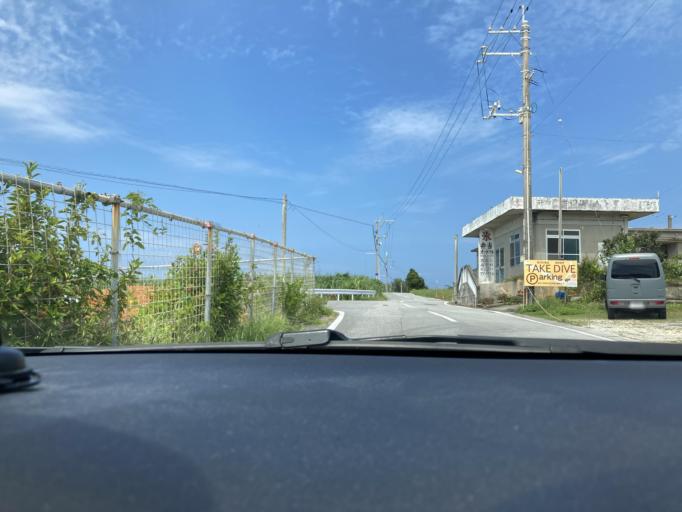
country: JP
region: Okinawa
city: Ishikawa
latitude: 26.4402
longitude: 127.7710
